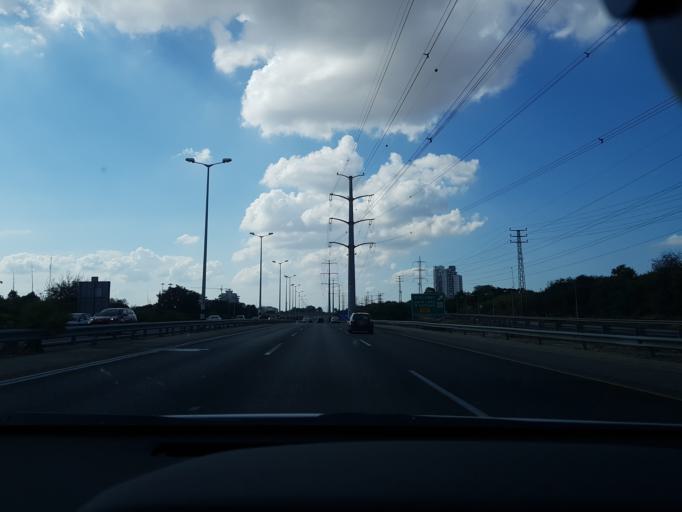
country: IL
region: Central District
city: Rishon LeZiyyon
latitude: 31.9816
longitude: 34.7942
